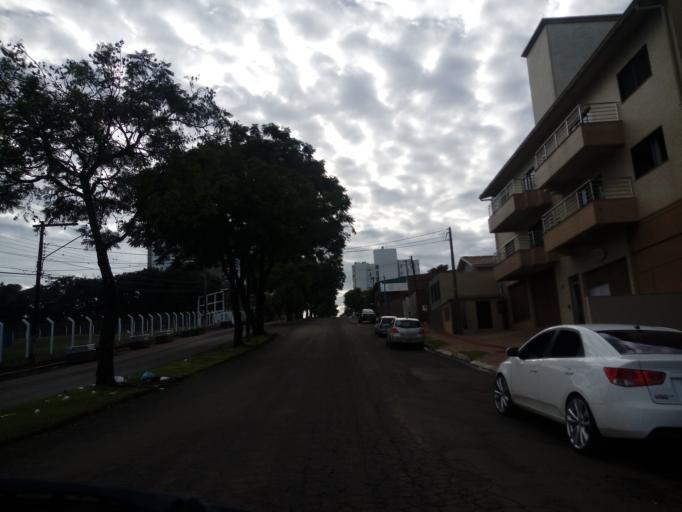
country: BR
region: Santa Catarina
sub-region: Chapeco
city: Chapeco
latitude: -27.1057
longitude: -52.6269
